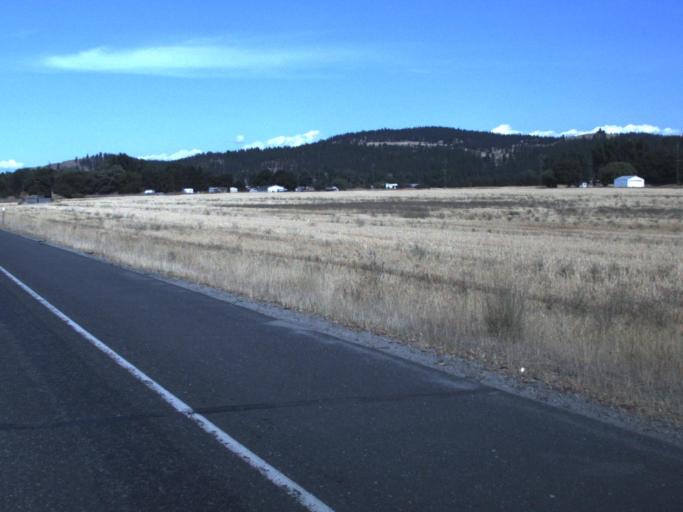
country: US
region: Washington
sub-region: Stevens County
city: Colville
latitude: 48.4474
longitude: -117.8720
